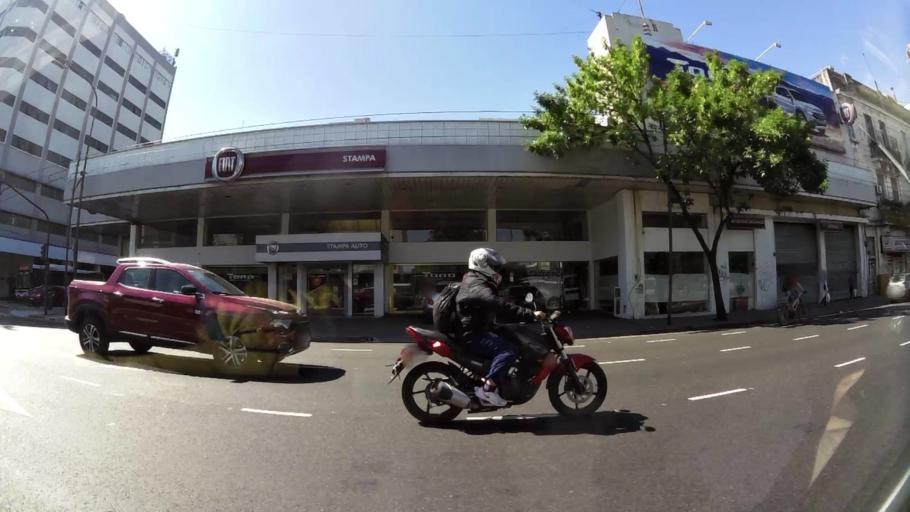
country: AR
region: Buenos Aires F.D.
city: Buenos Aires
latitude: -34.6226
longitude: -58.3895
